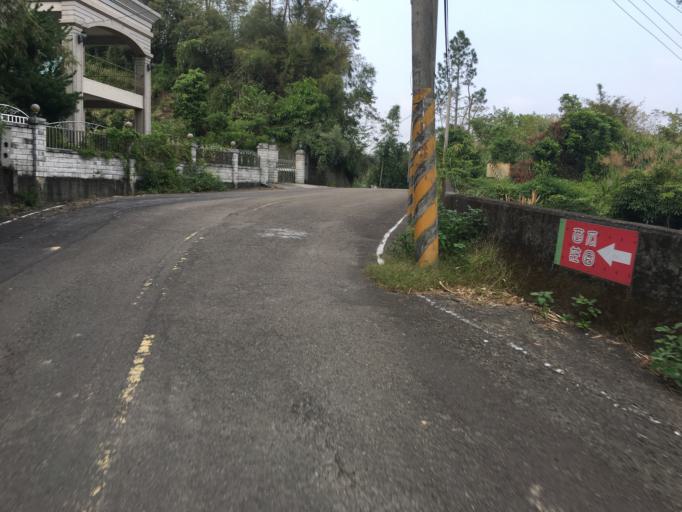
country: TW
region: Taiwan
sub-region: Hsinchu
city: Hsinchu
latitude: 24.7121
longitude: 121.0591
